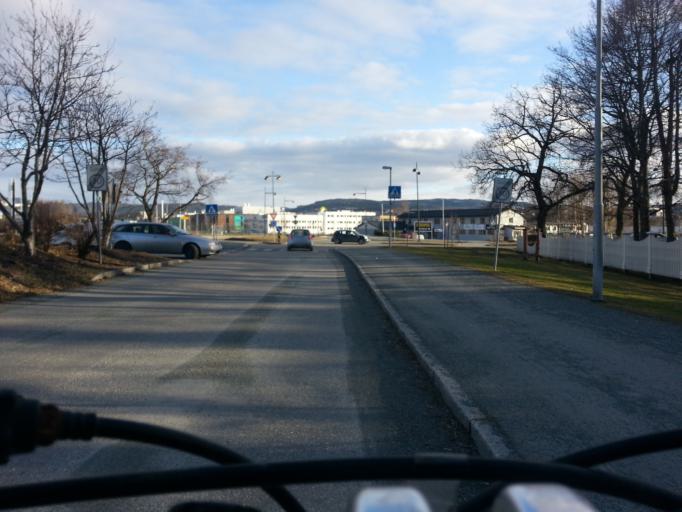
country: NO
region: Sor-Trondelag
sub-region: Trondheim
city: Trondheim
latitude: 63.4468
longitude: 10.4425
